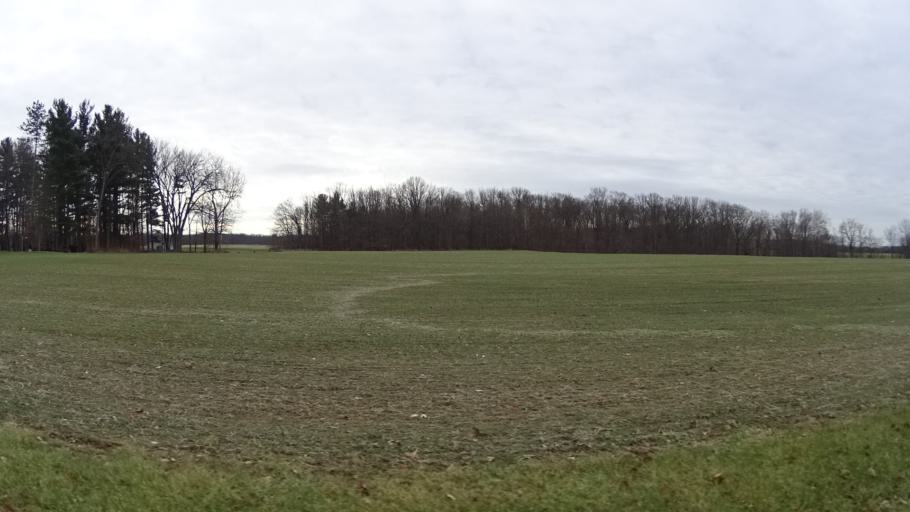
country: US
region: Ohio
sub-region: Lorain County
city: Wellington
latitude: 41.1478
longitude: -82.2068
